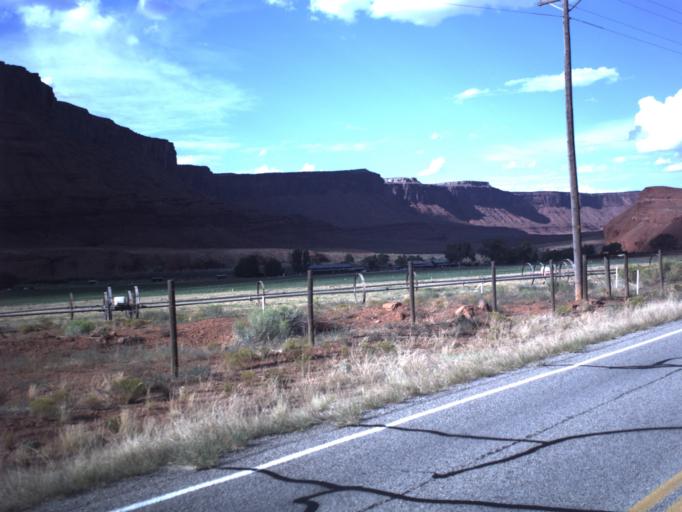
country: US
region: Utah
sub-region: Grand County
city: Moab
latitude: 38.6958
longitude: -109.4014
